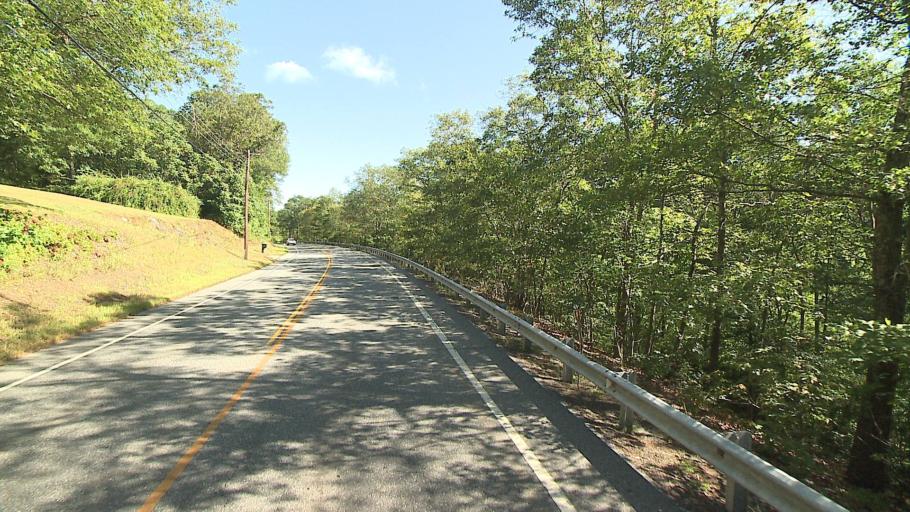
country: US
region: Connecticut
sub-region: New London County
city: Lisbon
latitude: 41.5653
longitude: -72.0133
